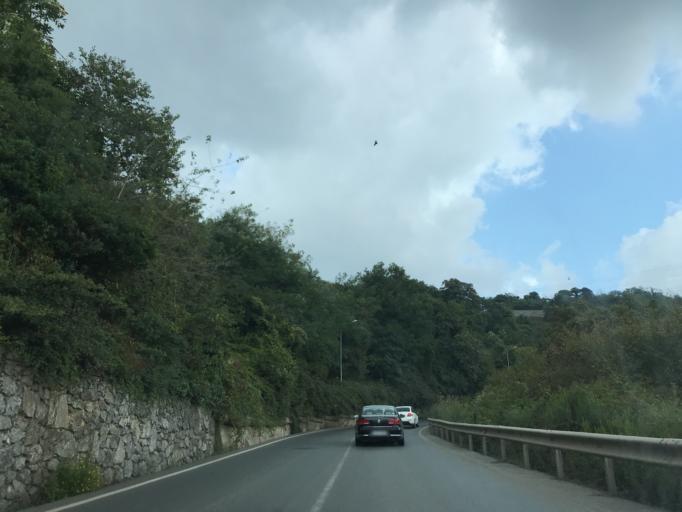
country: TR
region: Istanbul
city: Arikoey
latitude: 41.1825
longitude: 29.0451
